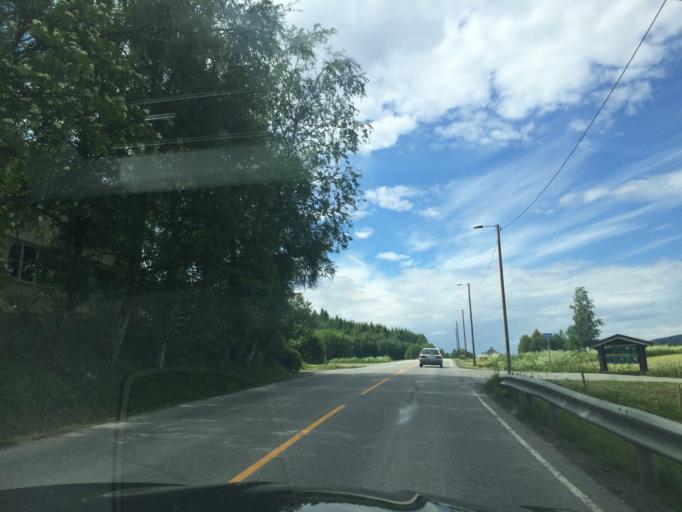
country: NO
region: Sor-Trondelag
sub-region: Selbu
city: Mebonden
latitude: 63.2404
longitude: 11.0685
